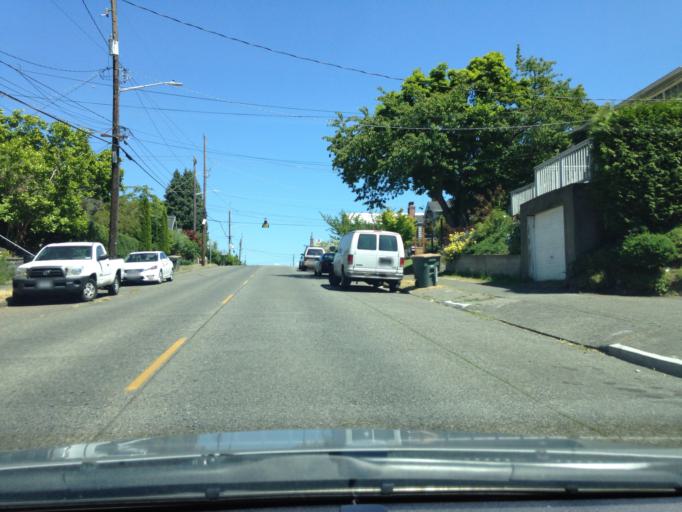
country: US
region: Washington
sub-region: King County
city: Mercer Island
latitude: 47.5512
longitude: -122.2820
